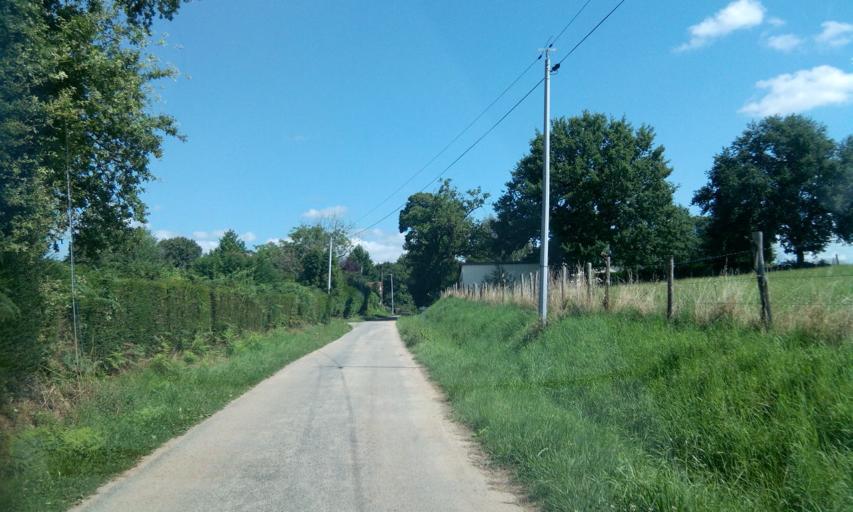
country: FR
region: Limousin
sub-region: Departement de la Haute-Vienne
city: Saint-Leonard-de-Noblat
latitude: 45.8175
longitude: 1.4731
